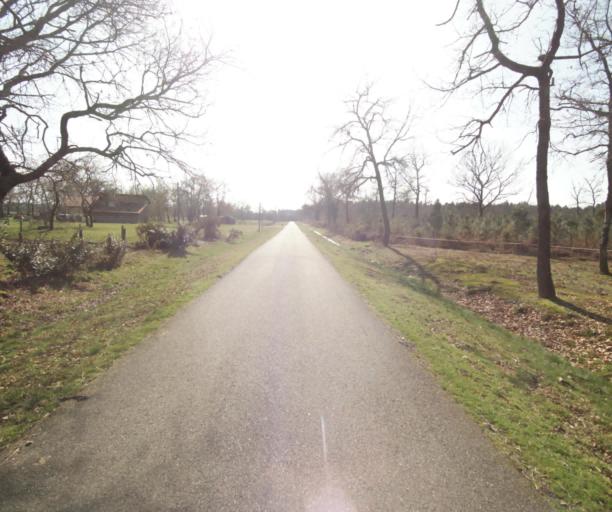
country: FR
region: Aquitaine
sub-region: Departement des Landes
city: Roquefort
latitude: 44.1523
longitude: -0.2508
